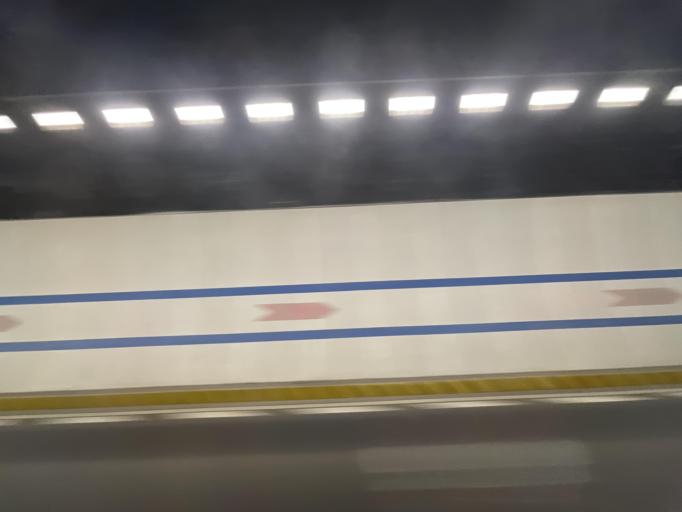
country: CN
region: Guangdong
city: Humen
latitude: 22.8066
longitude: 113.6540
